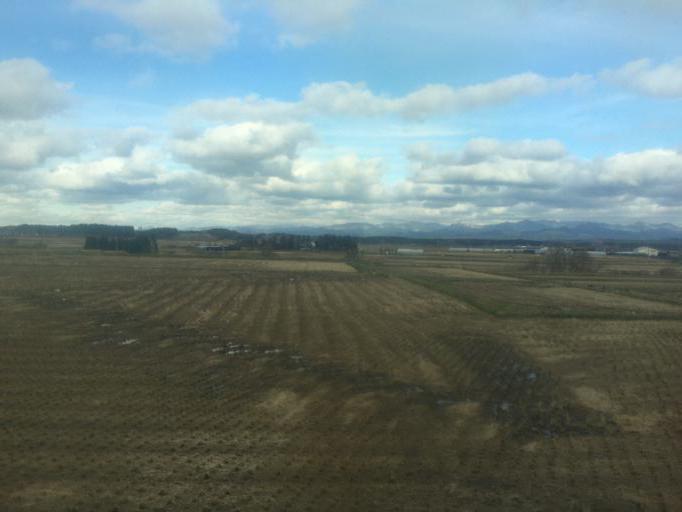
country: JP
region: Akita
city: Noshiromachi
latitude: 40.1955
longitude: 140.0965
